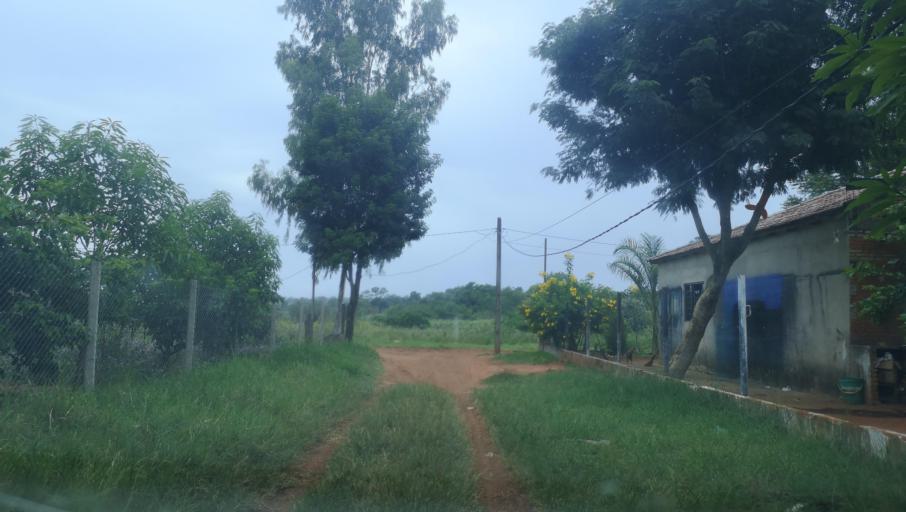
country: PY
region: San Pedro
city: Capiibary
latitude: -24.7291
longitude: -56.0121
